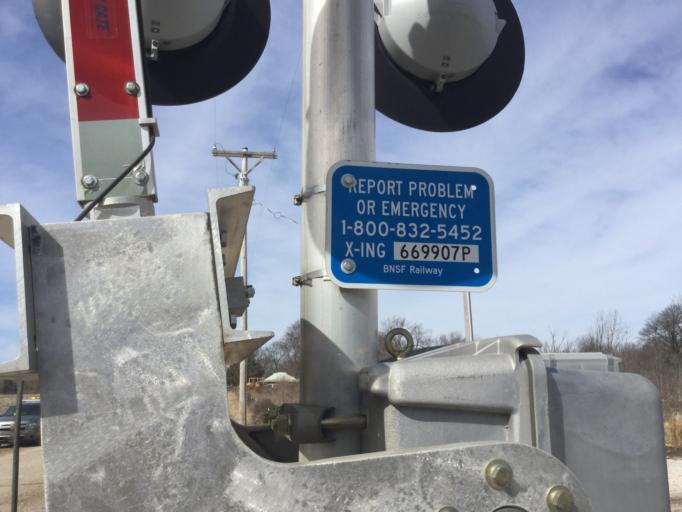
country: US
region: Kansas
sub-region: Cherokee County
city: Columbus
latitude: 37.2225
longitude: -94.8284
